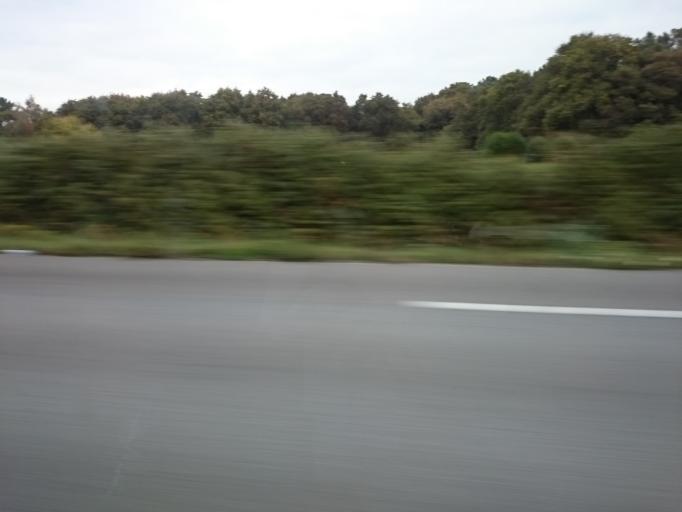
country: FR
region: Brittany
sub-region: Departement du Morbihan
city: Landaul
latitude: 47.7214
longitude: -3.0703
